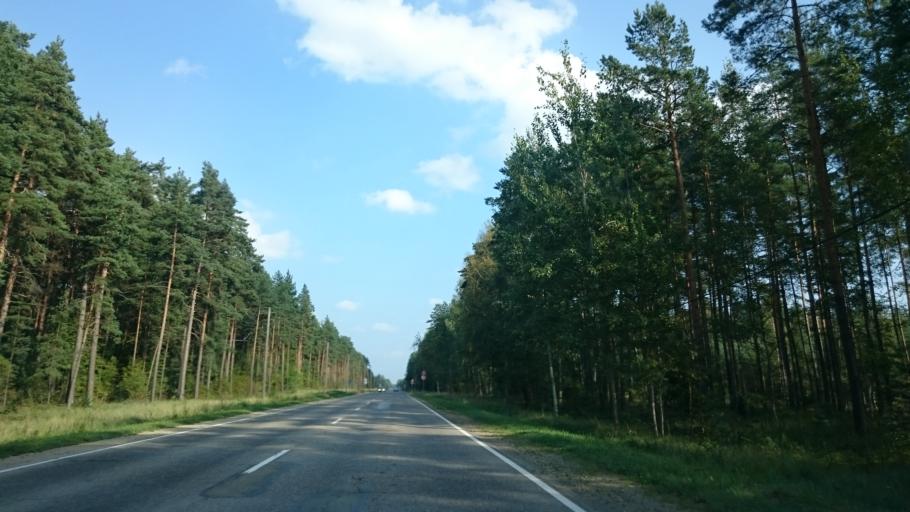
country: LV
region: Stopini
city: Ulbroka
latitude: 56.9454
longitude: 24.3038
